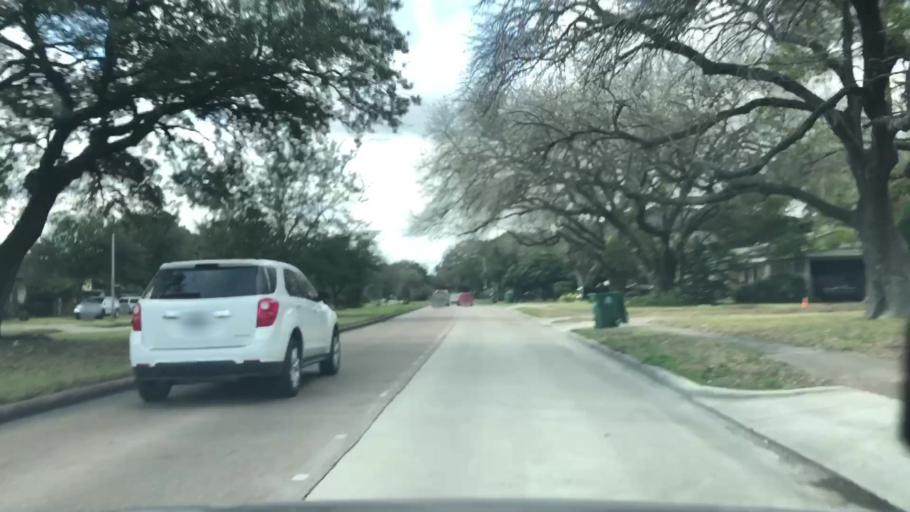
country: US
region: Texas
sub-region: Harris County
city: Bellaire
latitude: 29.6892
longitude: -95.4781
